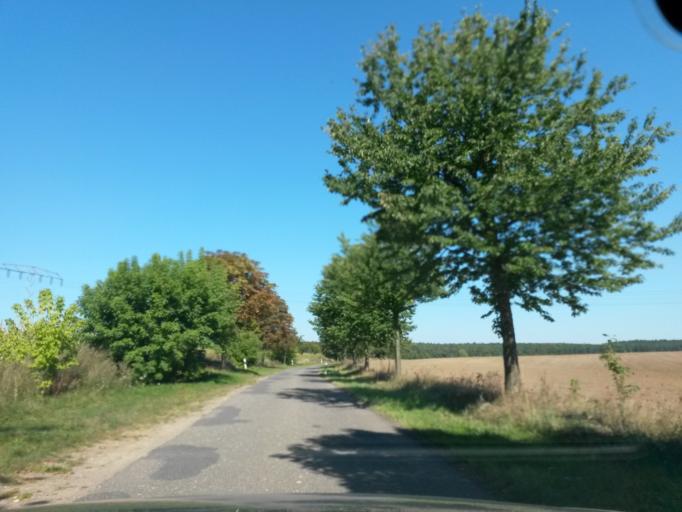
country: DE
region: Brandenburg
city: Templin
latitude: 53.1786
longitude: 13.4398
